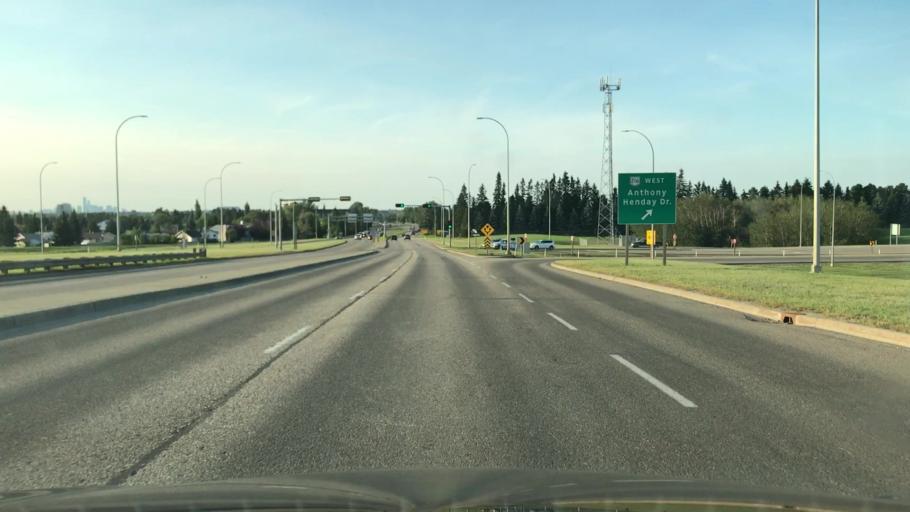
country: CA
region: Alberta
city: Beaumont
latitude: 53.4364
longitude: -113.4179
